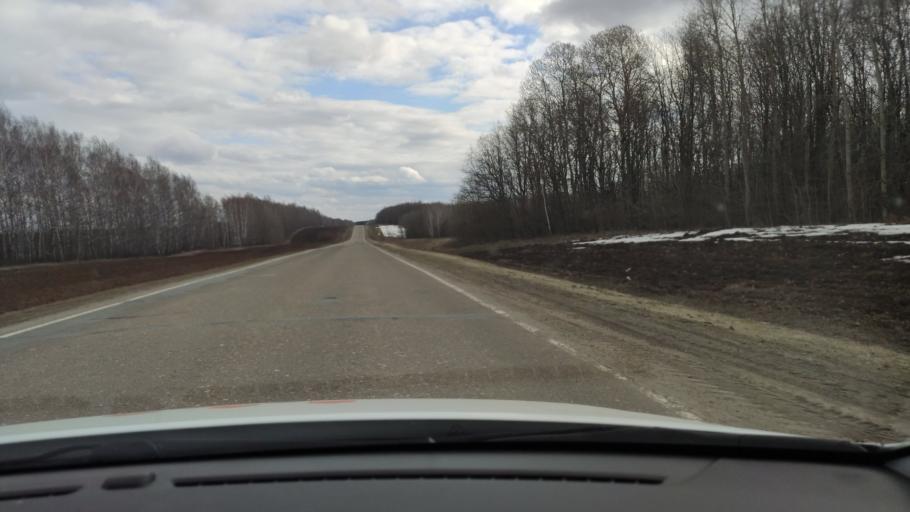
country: RU
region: Tatarstan
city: Vysokaya Gora
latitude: 56.0832
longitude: 49.1850
